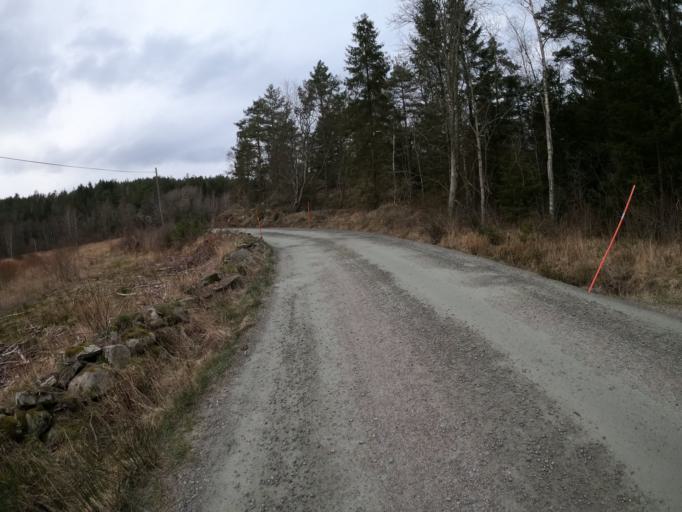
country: SE
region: Vaestra Goetaland
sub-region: Harryda Kommun
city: Molnlycke
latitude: 57.6342
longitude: 12.1020
